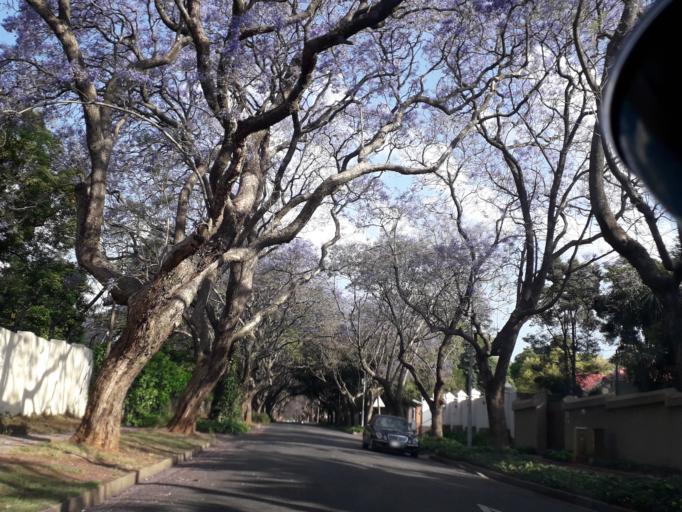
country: ZA
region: Gauteng
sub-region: City of Johannesburg Metropolitan Municipality
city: Johannesburg
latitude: -26.1367
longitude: 28.0762
